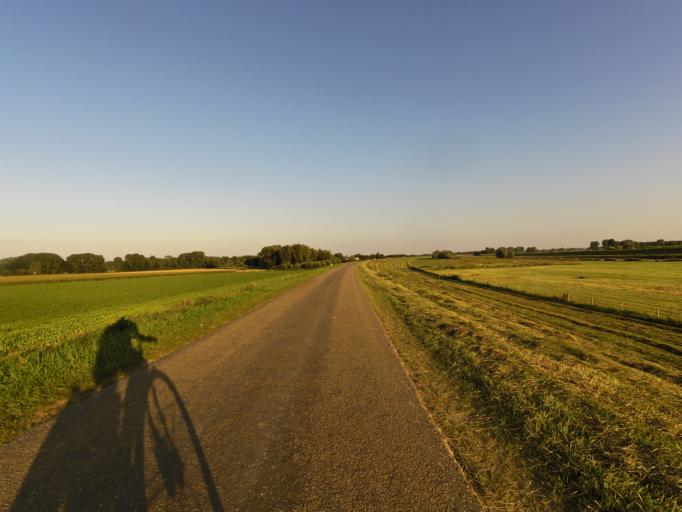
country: NL
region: Gelderland
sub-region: Gemeente Duiven
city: Duiven
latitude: 51.9041
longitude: 6.0182
